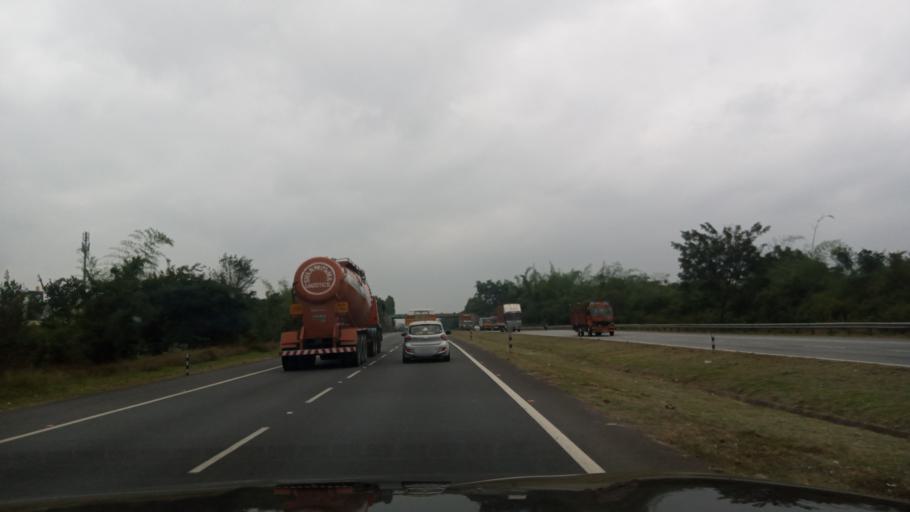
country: IN
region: Karnataka
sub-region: Bangalore Rural
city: Nelamangala
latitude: 13.0290
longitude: 77.4755
